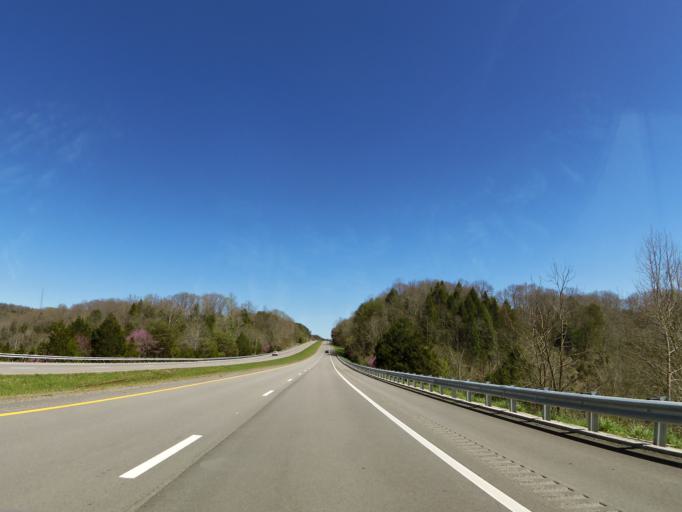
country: US
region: Kentucky
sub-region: Casey County
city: Liberty
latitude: 37.1005
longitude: -84.8503
